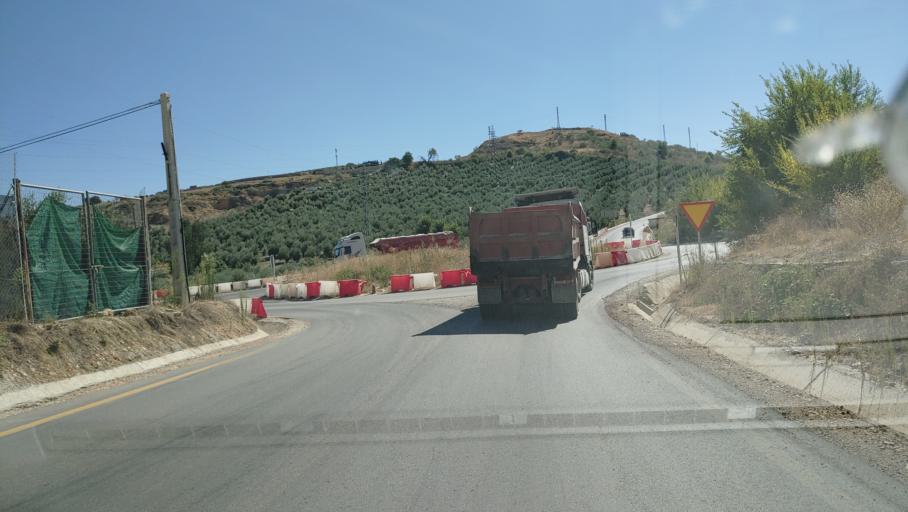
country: ES
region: Andalusia
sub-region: Provincia de Jaen
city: Villanueva del Arzobispo
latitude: 38.1627
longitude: -2.9924
